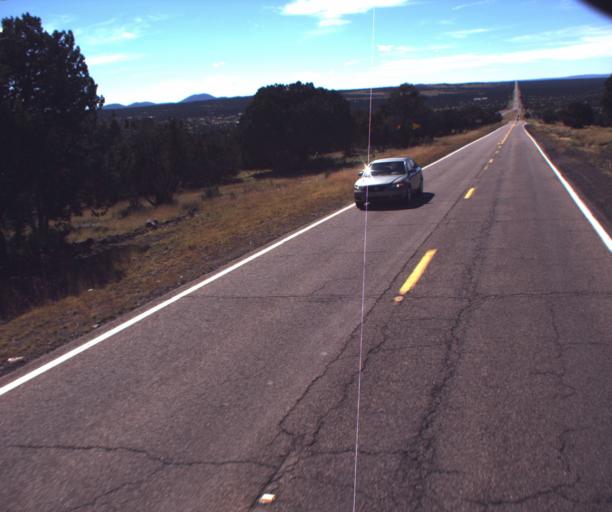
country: US
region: Arizona
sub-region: Navajo County
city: White Mountain Lake
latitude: 34.2882
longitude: -109.8242
